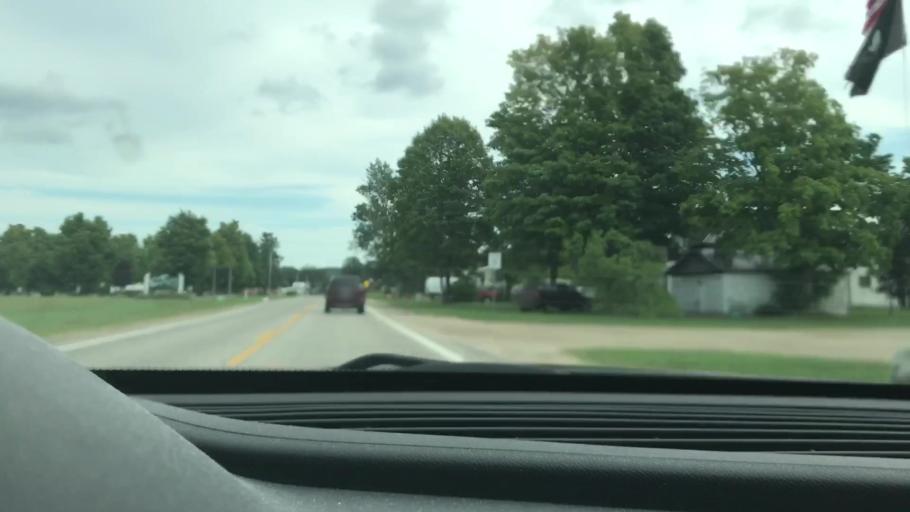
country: US
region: Michigan
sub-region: Antrim County
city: Mancelona
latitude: 44.9022
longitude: -85.0757
